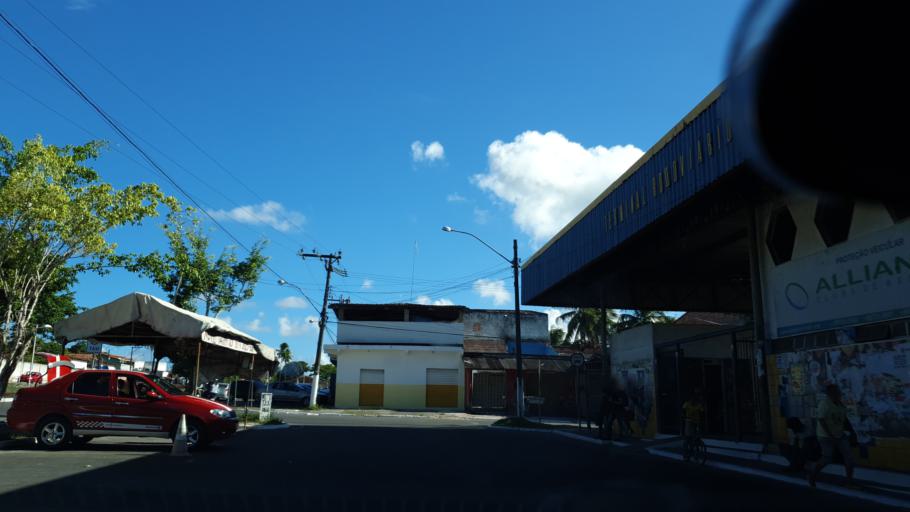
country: BR
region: Bahia
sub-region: Mata De Sao Joao
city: Mata de Sao Joao
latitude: -12.6107
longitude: -38.2979
